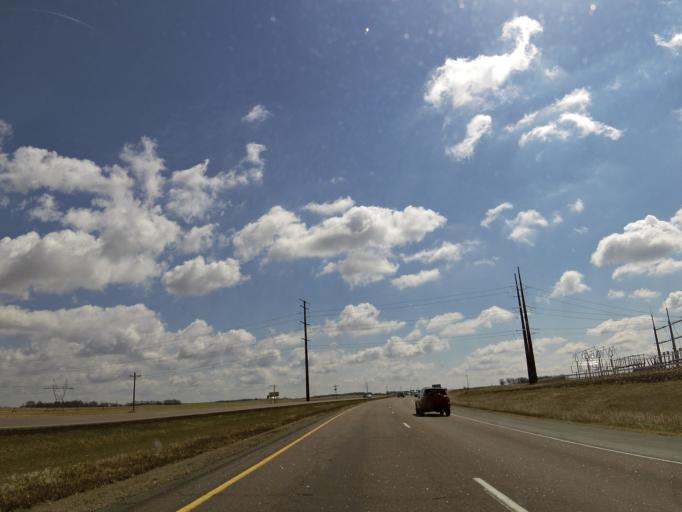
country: US
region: Minnesota
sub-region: Dakota County
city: Farmington
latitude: 44.6406
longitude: -92.9951
